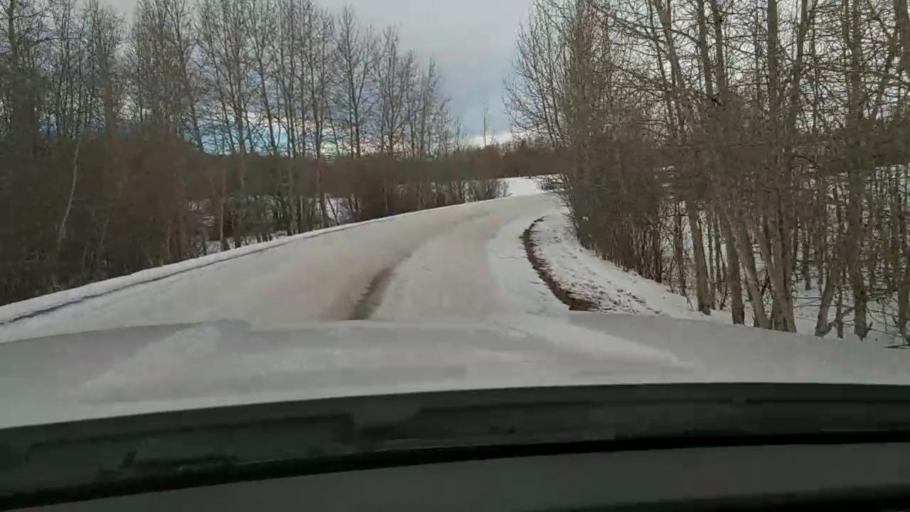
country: CA
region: Alberta
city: Cochrane
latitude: 51.1989
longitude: -114.2858
